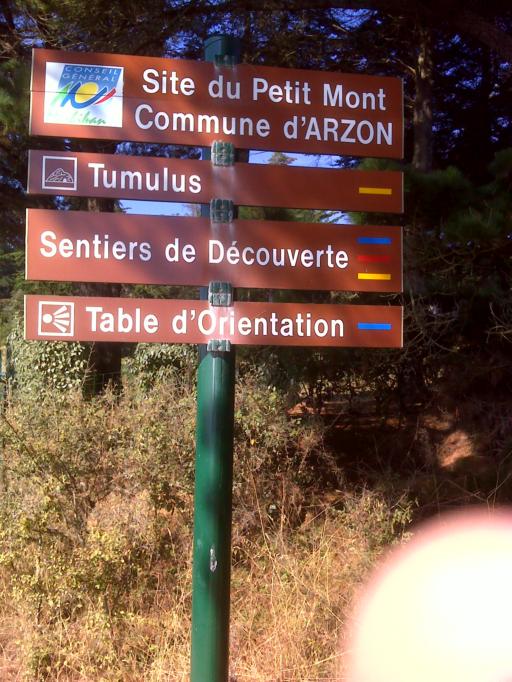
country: FR
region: Brittany
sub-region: Departement du Morbihan
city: Arzon
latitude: 47.5383
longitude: -2.8956
